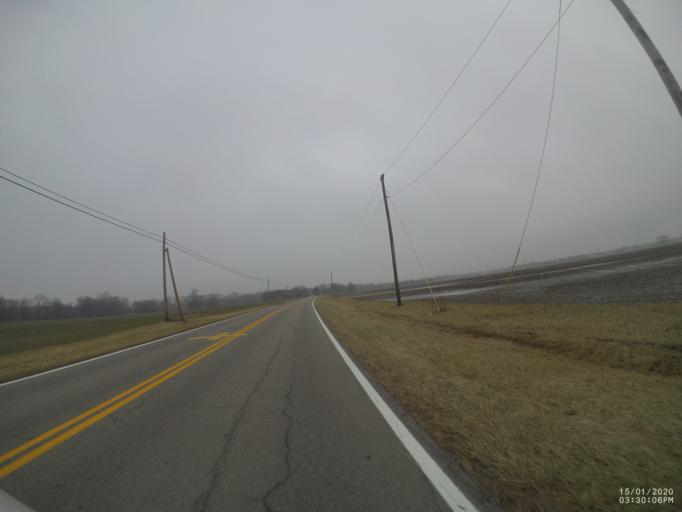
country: US
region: Ohio
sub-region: Sandusky County
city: Woodville
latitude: 41.4441
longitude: -83.3839
